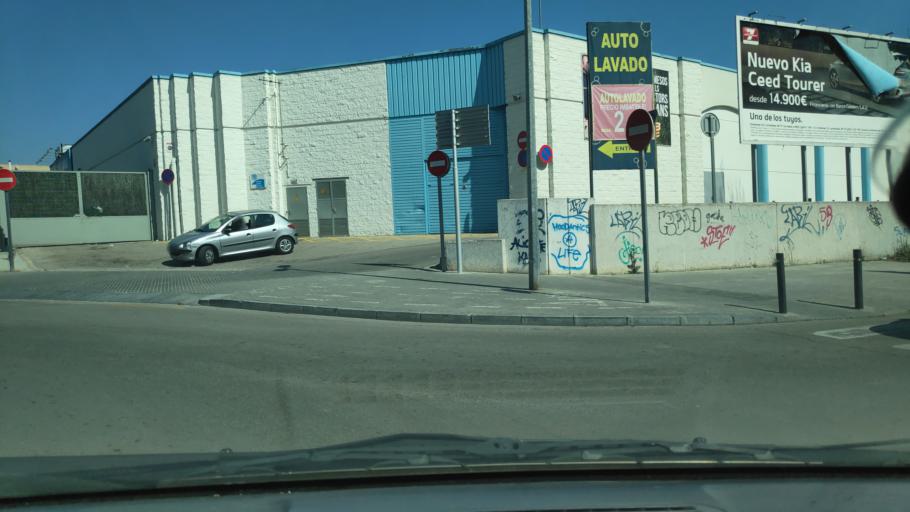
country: ES
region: Catalonia
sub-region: Provincia de Barcelona
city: Mollet del Valles
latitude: 41.5370
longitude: 2.2181
